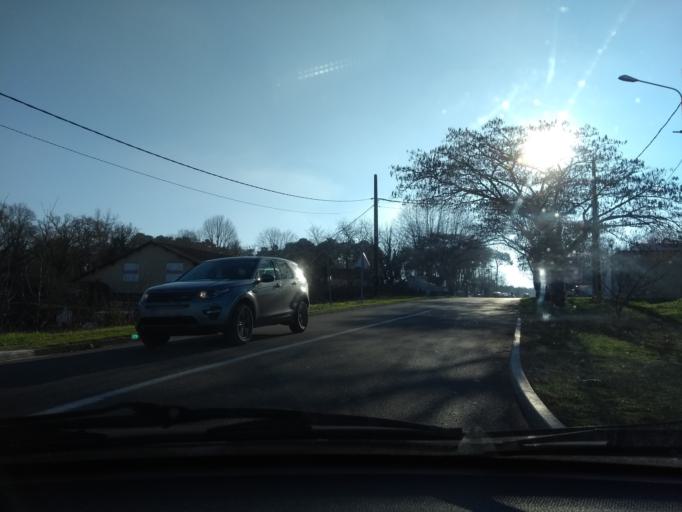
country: FR
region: Aquitaine
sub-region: Departement de la Gironde
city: Salles
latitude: 44.5472
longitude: -0.8732
